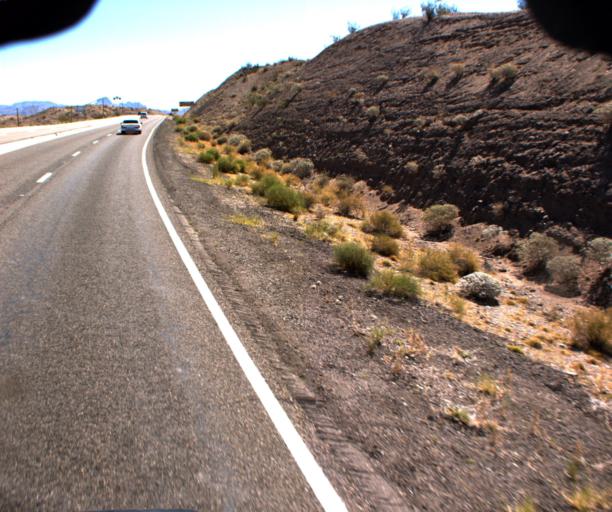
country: US
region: Nevada
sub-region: Clark County
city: Laughlin
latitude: 35.1853
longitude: -114.5609
